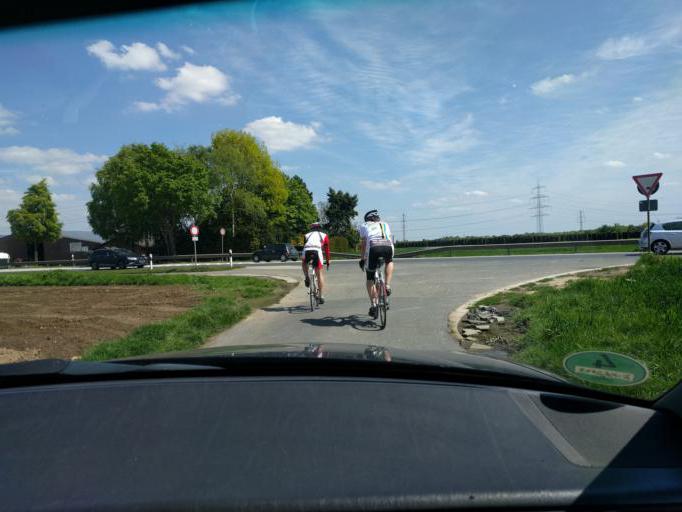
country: DE
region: North Rhine-Westphalia
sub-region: Regierungsbezirk Dusseldorf
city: Kaarst
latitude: 51.2396
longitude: 6.6208
